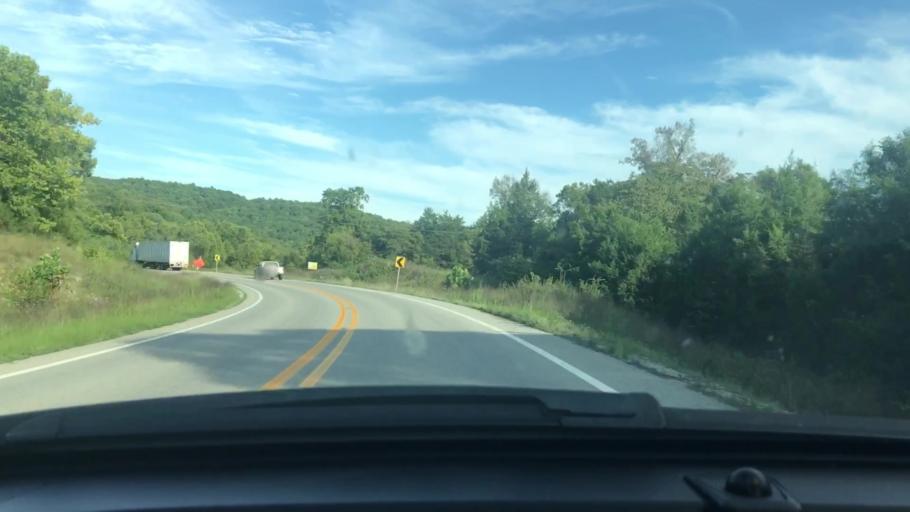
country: US
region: Arkansas
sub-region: Sharp County
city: Cherokee Village
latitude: 36.2973
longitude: -91.4363
